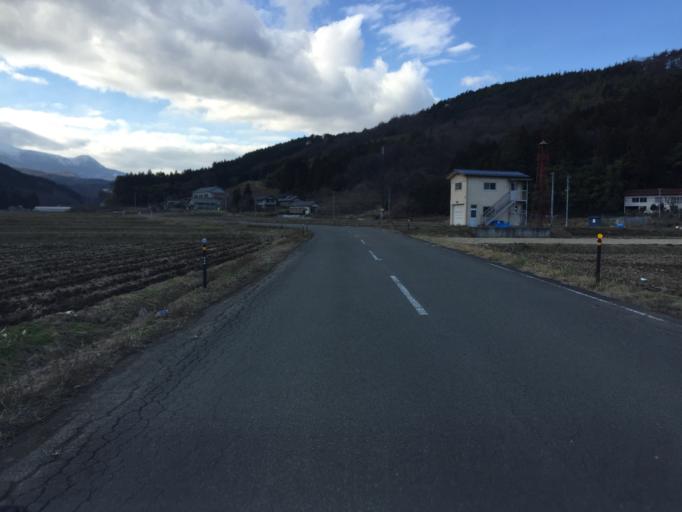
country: JP
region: Fukushima
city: Nihommatsu
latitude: 37.6725
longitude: 140.4090
